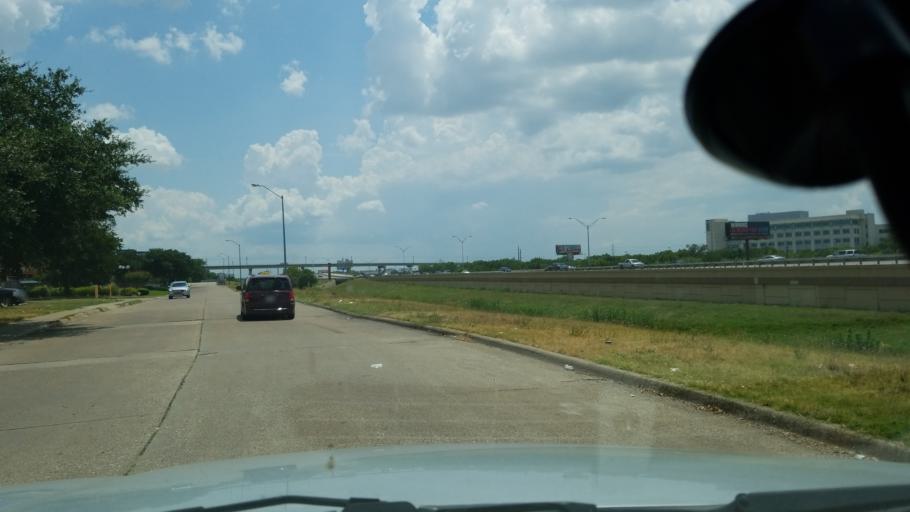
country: US
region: Texas
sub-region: Dallas County
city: Farmers Branch
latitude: 32.8591
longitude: -96.8897
